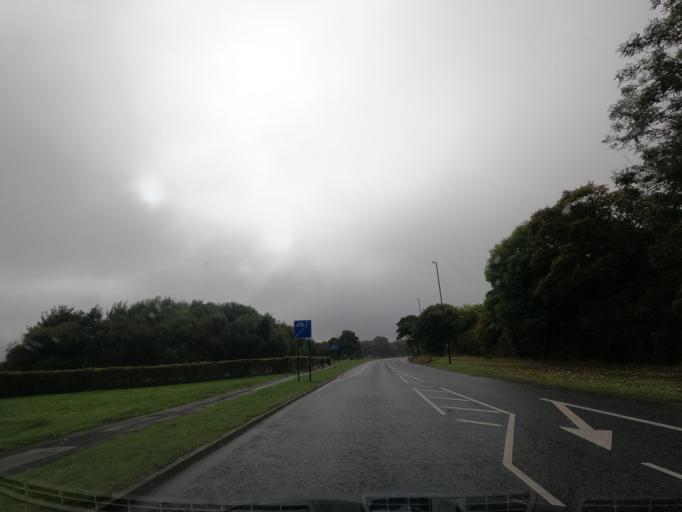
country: GB
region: England
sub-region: Redcar and Cleveland
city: Redcar
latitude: 54.5937
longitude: -1.0828
